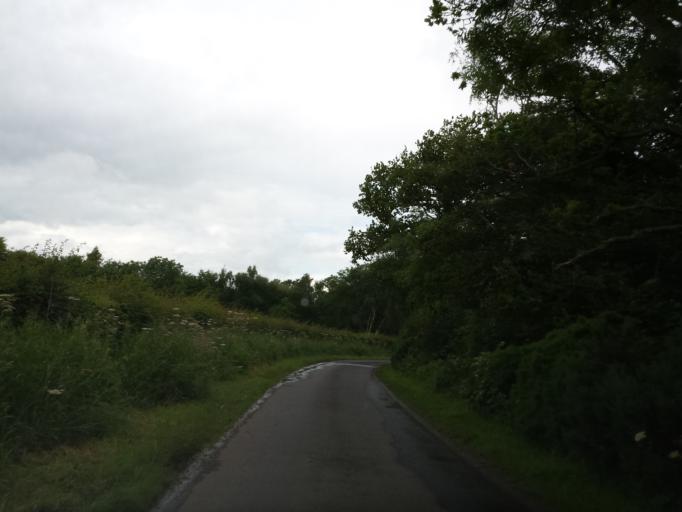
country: GB
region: Scotland
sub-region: The Scottish Borders
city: Saint Boswells
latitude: 55.6085
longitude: -2.5618
